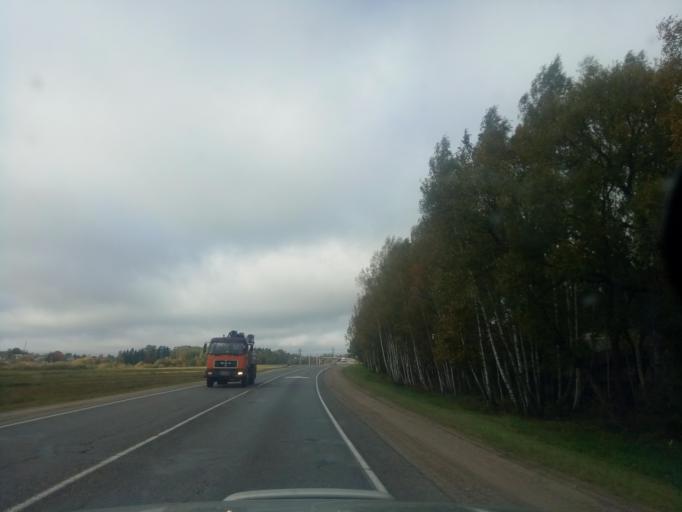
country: BY
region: Minsk
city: Zaslawye
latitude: 53.9941
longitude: 27.2940
